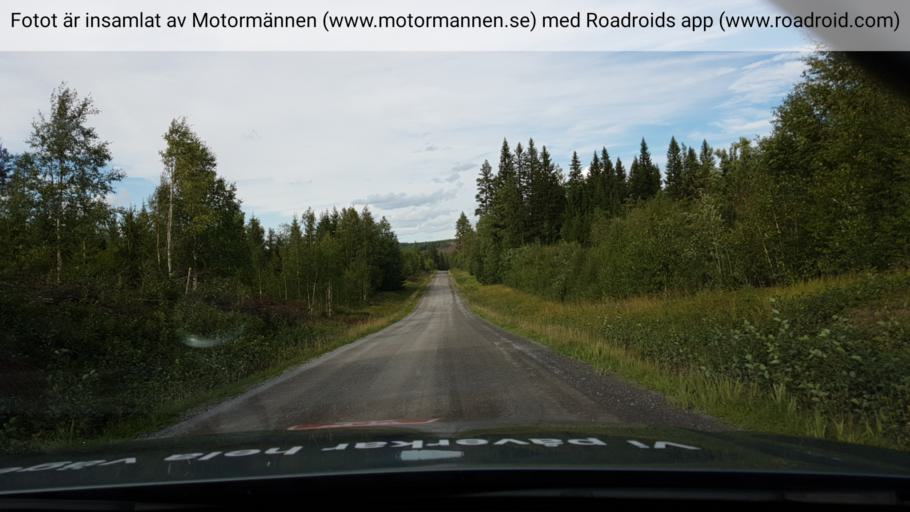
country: SE
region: Jaemtland
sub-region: Braecke Kommun
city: Braecke
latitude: 63.2571
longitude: 15.3727
